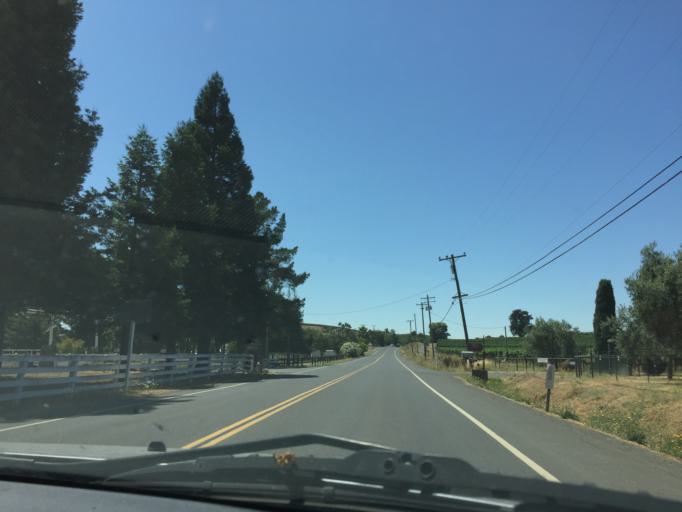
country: US
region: California
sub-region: Napa County
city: Napa
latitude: 38.2693
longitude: -122.3317
